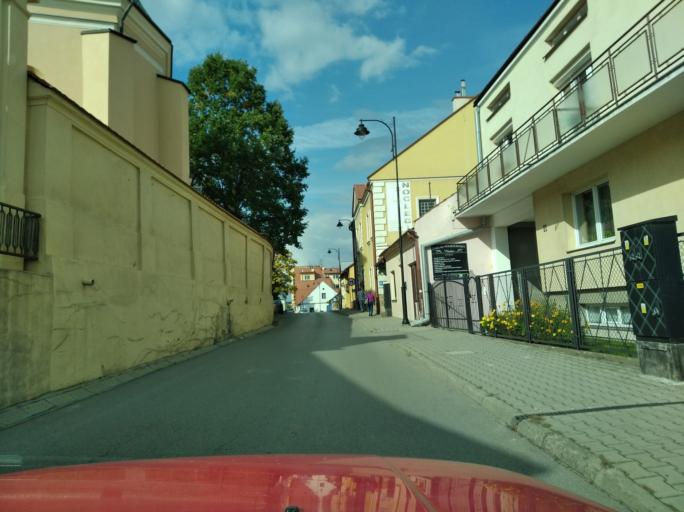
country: PL
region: Subcarpathian Voivodeship
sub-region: Powiat rzeszowski
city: Tyczyn
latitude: 49.9618
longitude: 22.0343
